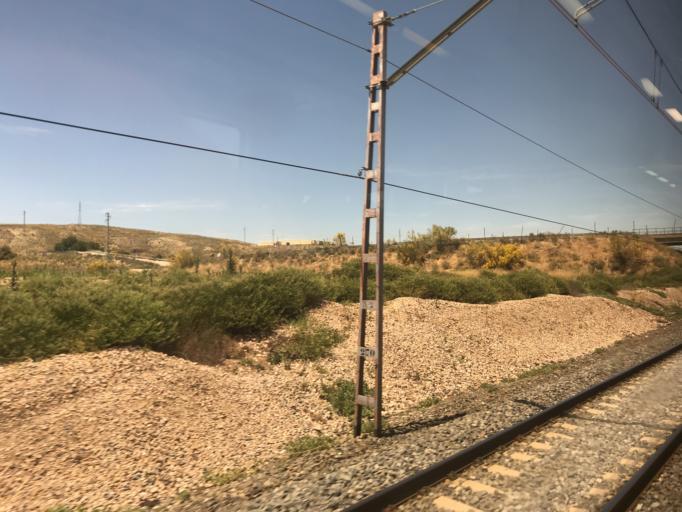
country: ES
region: Madrid
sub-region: Provincia de Madrid
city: Aranjuez
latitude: 40.0867
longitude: -3.6323
